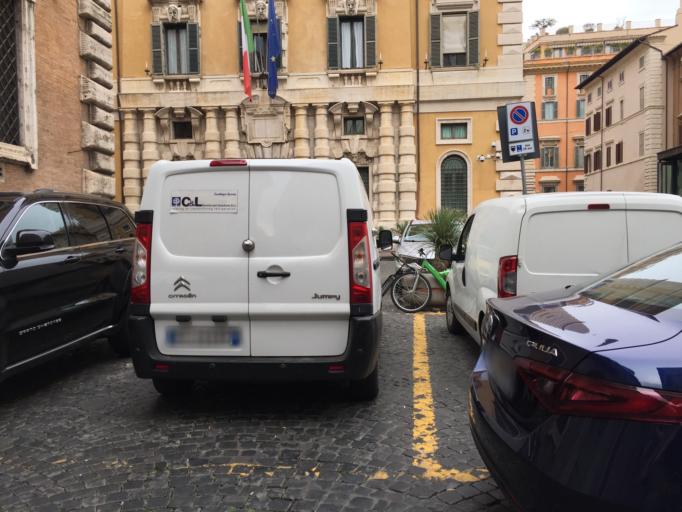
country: VA
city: Vatican City
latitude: 41.8983
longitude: 12.4751
